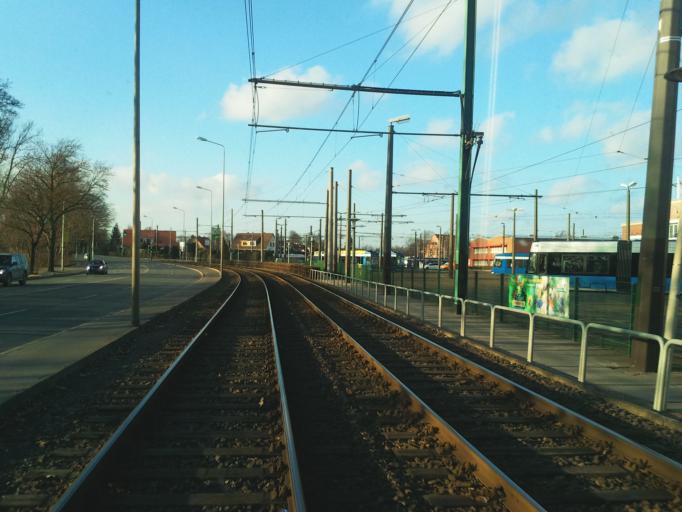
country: DE
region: Mecklenburg-Vorpommern
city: Rostock
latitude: 54.0976
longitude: 12.0914
